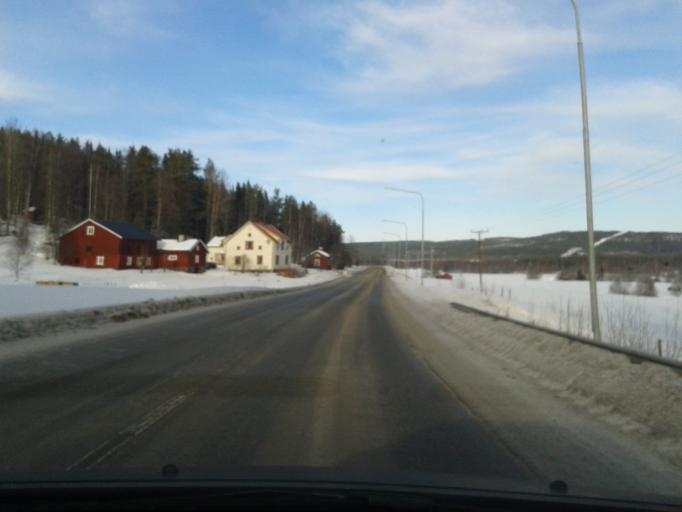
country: SE
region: Vaesternorrland
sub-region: OErnskoeldsviks Kommun
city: Bredbyn
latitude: 63.4932
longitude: 18.0802
